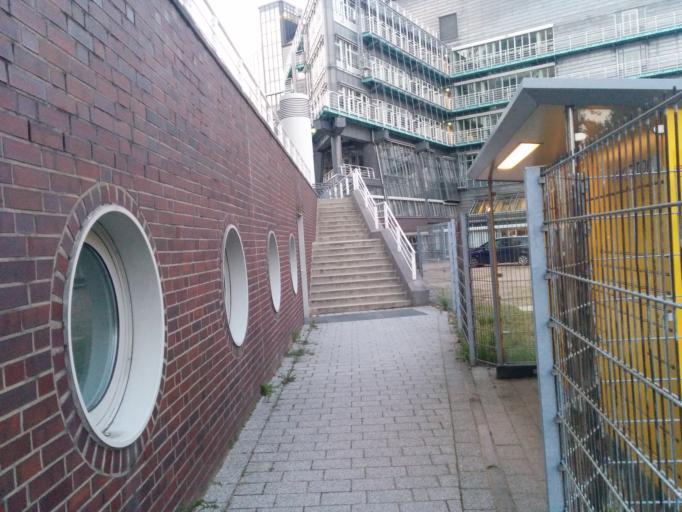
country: DE
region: Hamburg
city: Neustadt
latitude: 53.5453
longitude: 9.9800
